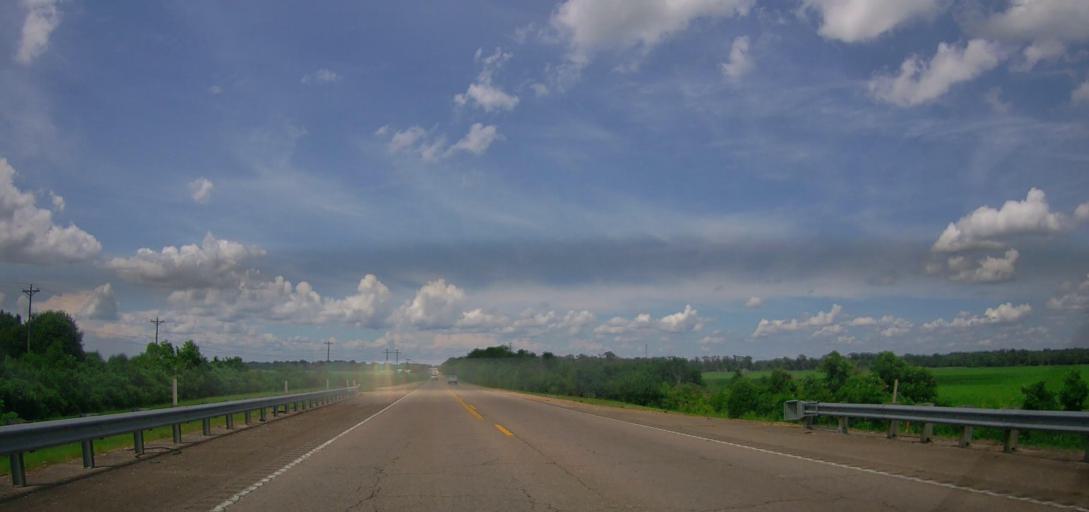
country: US
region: Mississippi
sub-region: Lee County
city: Shannon
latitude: 34.1389
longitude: -88.7194
